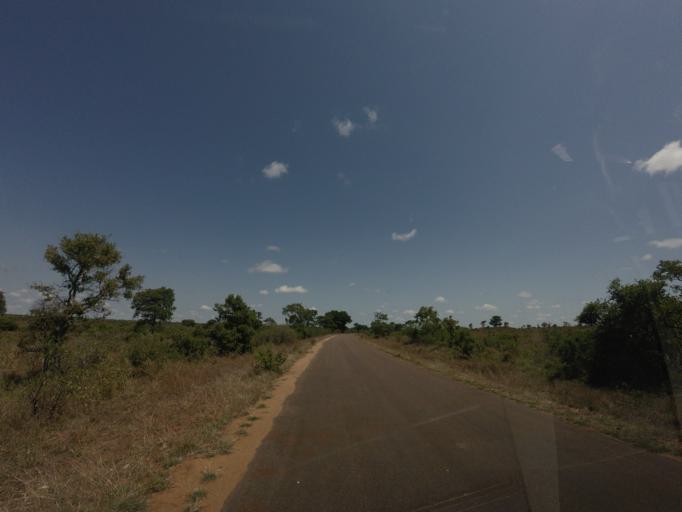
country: ZA
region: Mpumalanga
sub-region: Ehlanzeni District
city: Komatipoort
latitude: -24.9907
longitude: 31.9061
